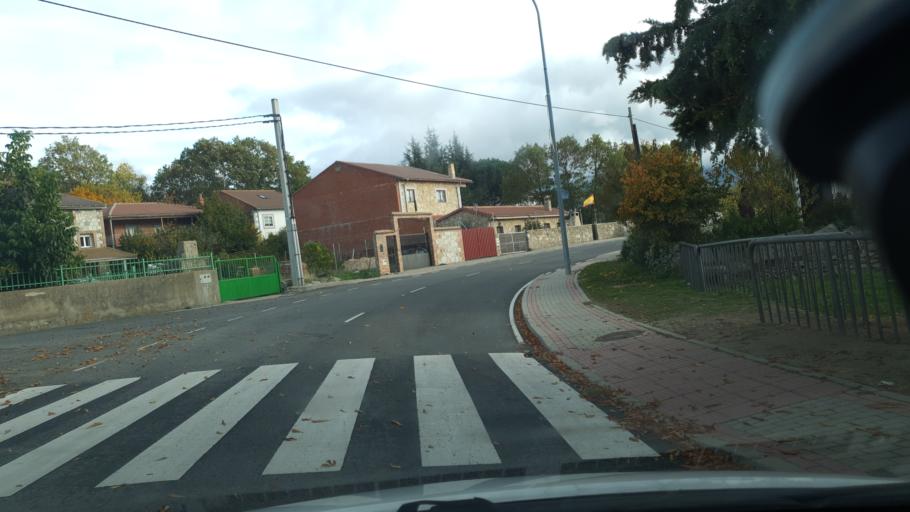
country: ES
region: Castille and Leon
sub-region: Provincia de Avila
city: Navalosa
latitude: 40.3996
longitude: -4.9310
